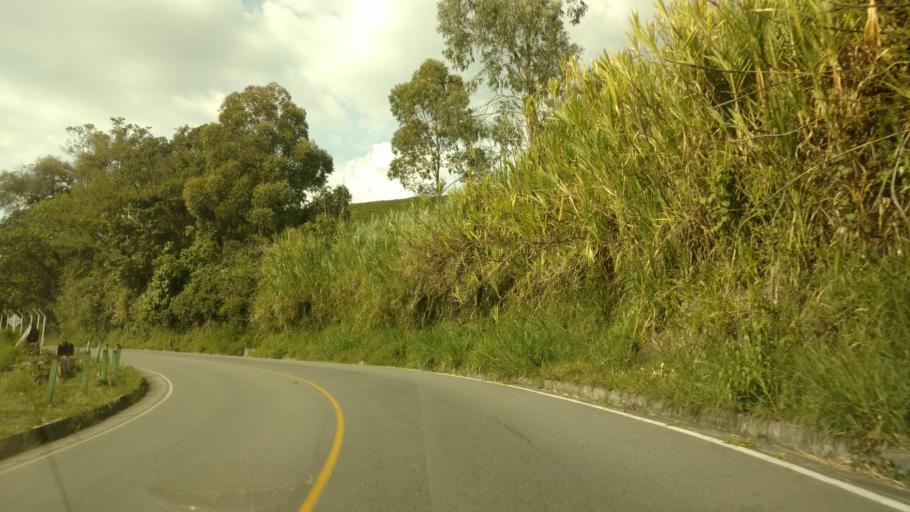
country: CO
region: Caldas
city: Neira
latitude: 5.1429
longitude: -75.5093
